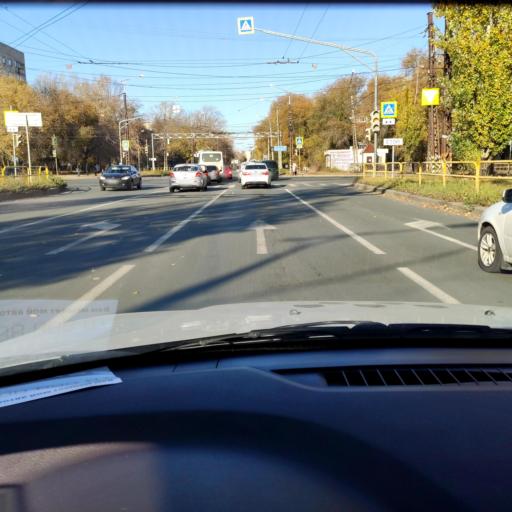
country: RU
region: Samara
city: Tol'yatti
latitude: 53.5094
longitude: 49.4308
